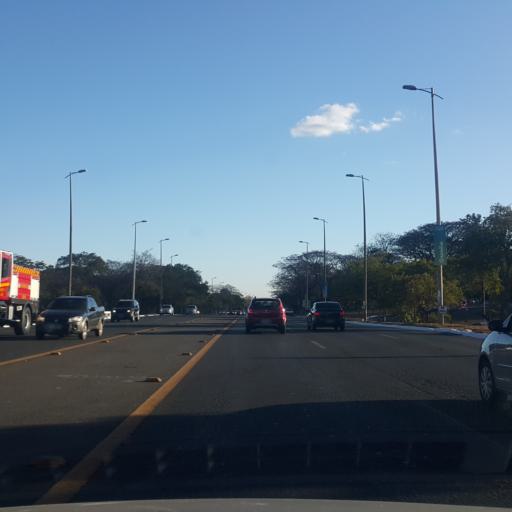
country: BR
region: Federal District
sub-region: Brasilia
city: Brasilia
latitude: -15.8077
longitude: -47.8908
